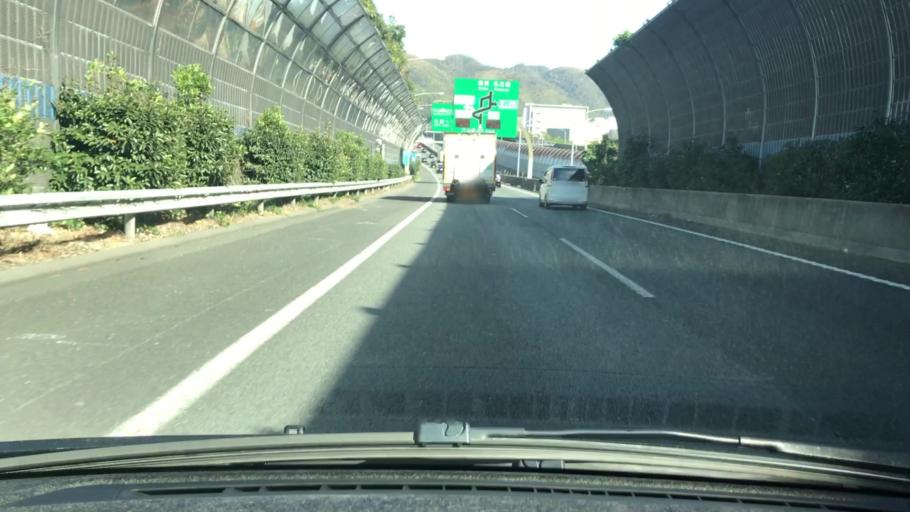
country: JP
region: Kyoto
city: Yawata
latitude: 34.8787
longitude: 135.6567
